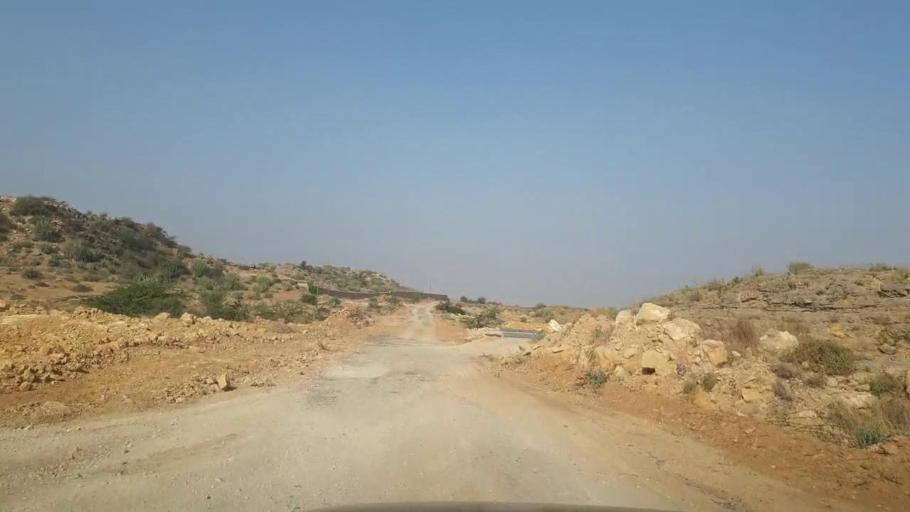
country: PK
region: Sindh
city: Gharo
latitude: 25.0487
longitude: 67.5458
